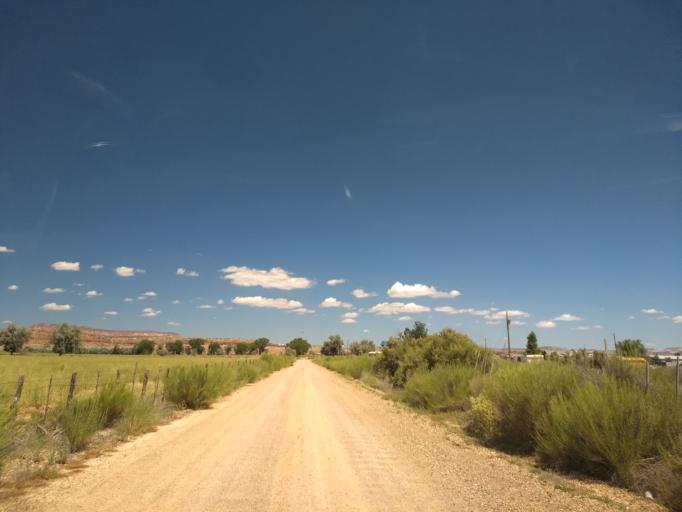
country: US
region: Arizona
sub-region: Coconino County
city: Fredonia
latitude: 36.9308
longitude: -112.5399
